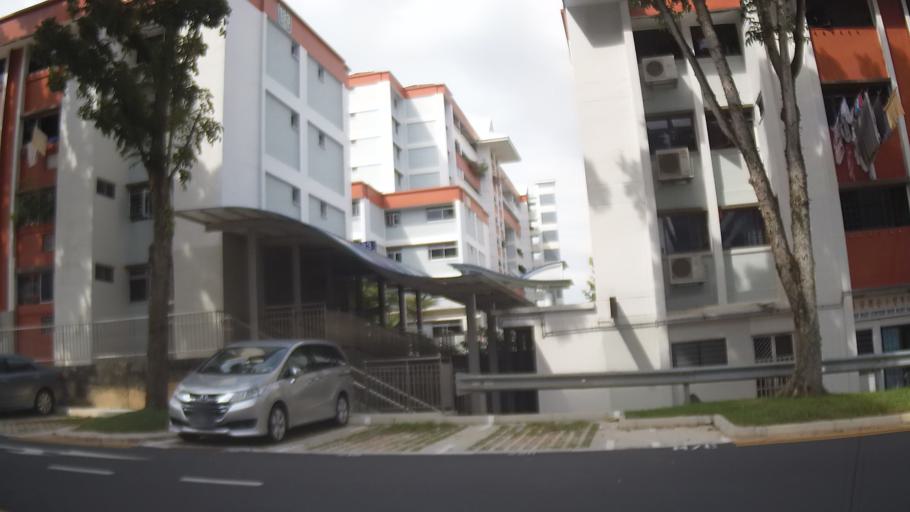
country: MY
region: Johor
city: Johor Bahru
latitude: 1.4380
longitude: 103.7783
